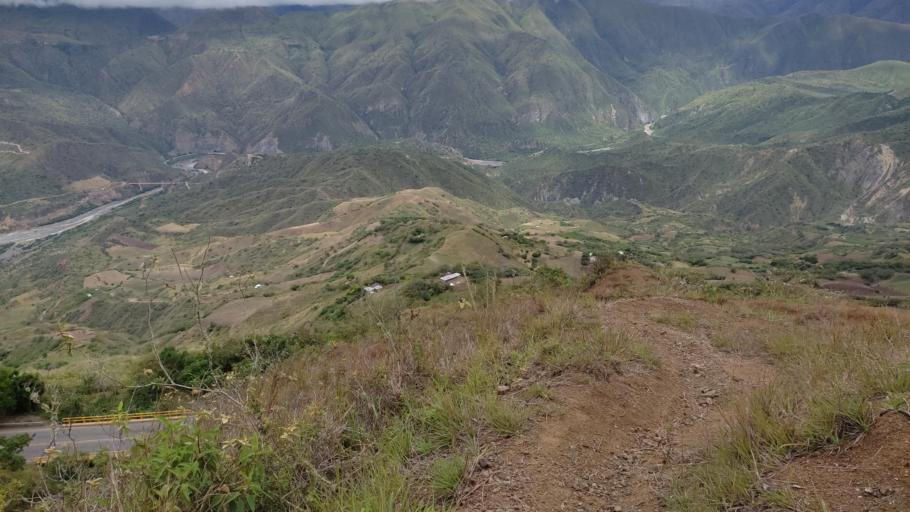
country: CO
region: Narino
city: Taminango
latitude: 1.5413
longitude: -77.3668
